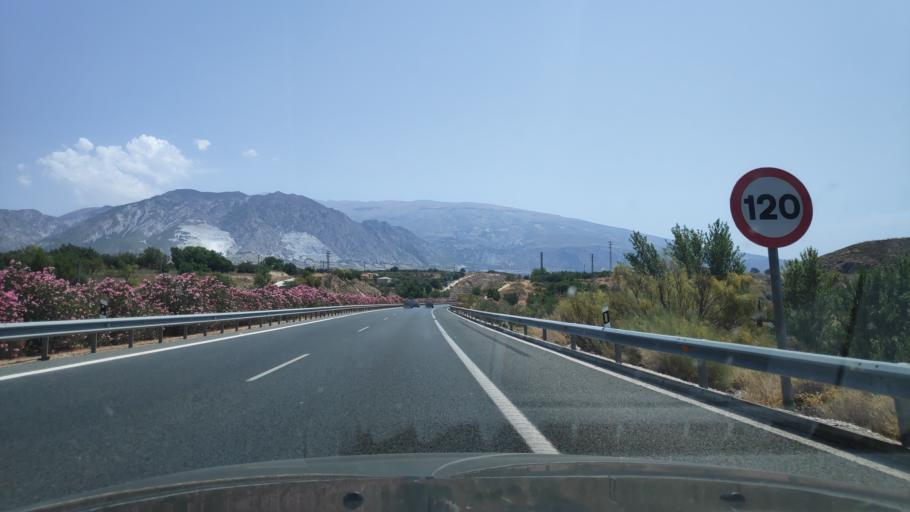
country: ES
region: Andalusia
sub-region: Provincia de Granada
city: Durcal
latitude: 36.9877
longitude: -3.5979
